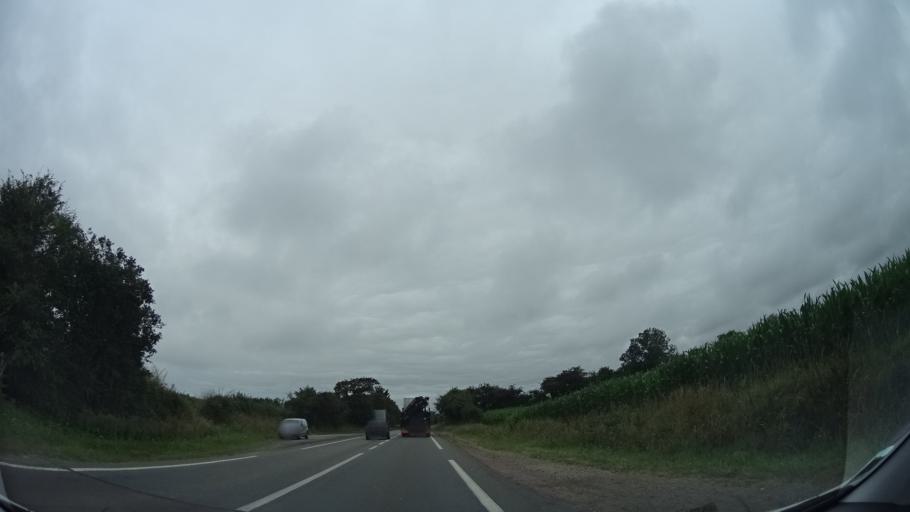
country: FR
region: Lower Normandy
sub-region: Departement de la Manche
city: Portbail
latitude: 49.3617
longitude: -1.6966
